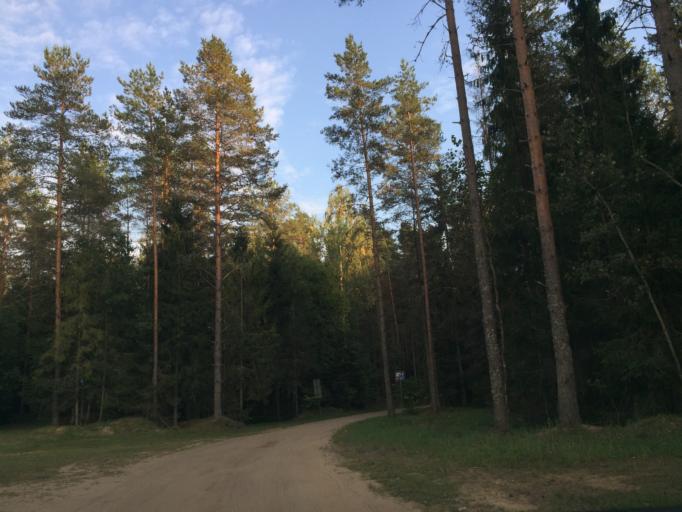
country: LV
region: Baldone
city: Baldone
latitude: 56.7687
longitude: 24.4036
